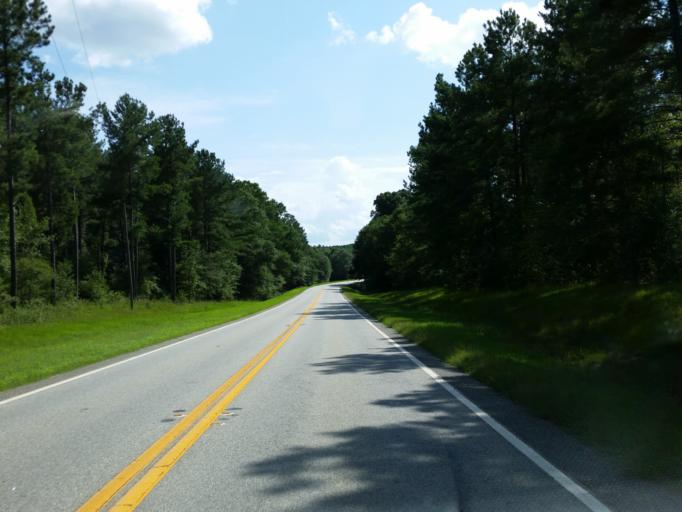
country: US
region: Georgia
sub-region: Turner County
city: Ashburn
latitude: 31.6937
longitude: -83.7007
